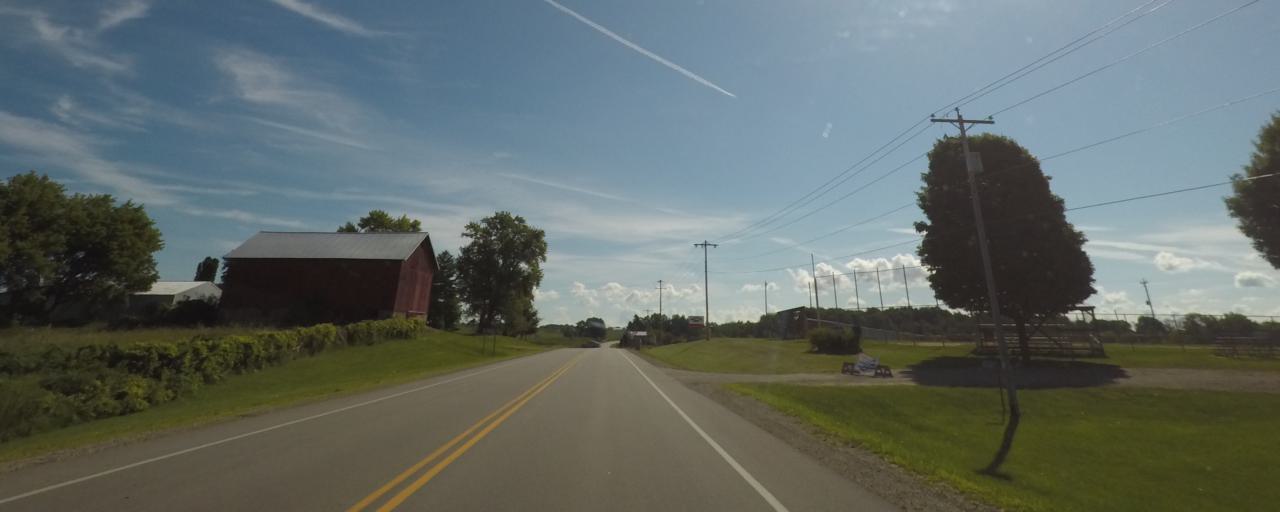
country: US
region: Wisconsin
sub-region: Jefferson County
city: Johnson Creek
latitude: 43.0733
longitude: -88.6843
